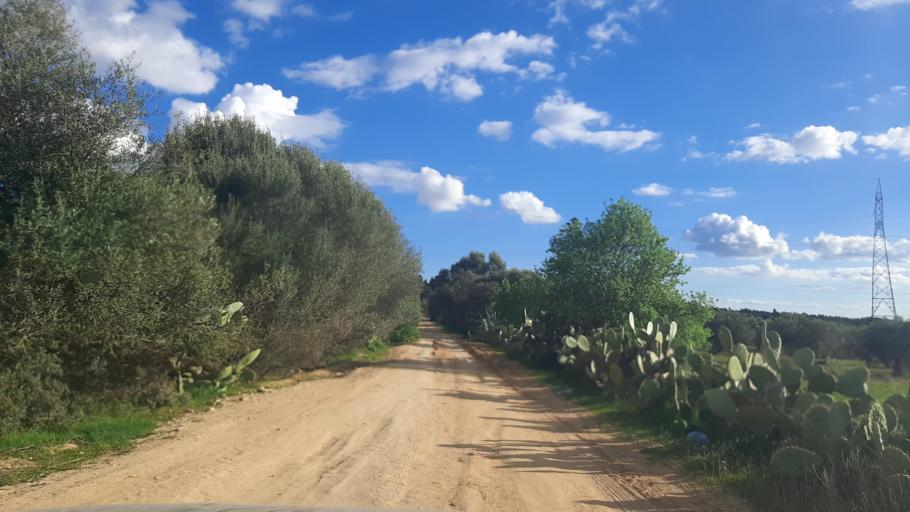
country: TN
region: Nabul
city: Bu `Urqub
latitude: 36.4407
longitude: 10.5075
